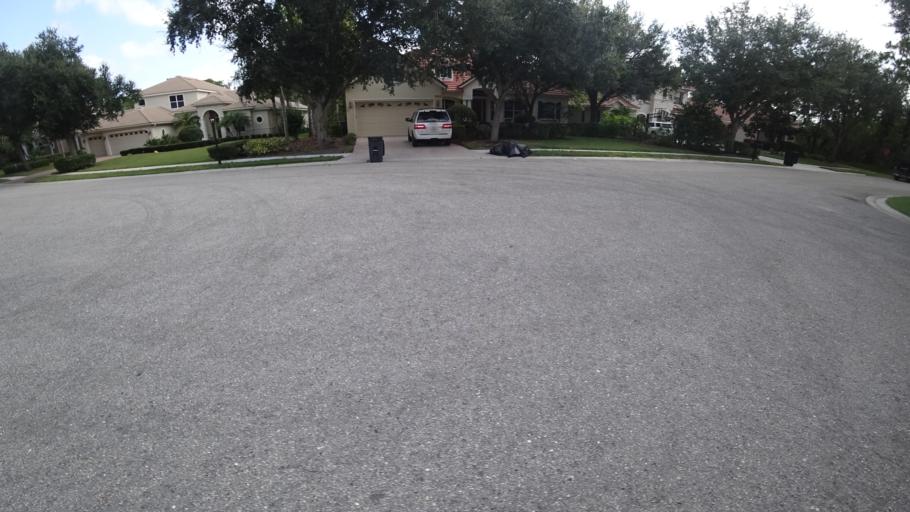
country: US
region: Florida
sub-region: Sarasota County
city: The Meadows
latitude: 27.4007
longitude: -82.4429
